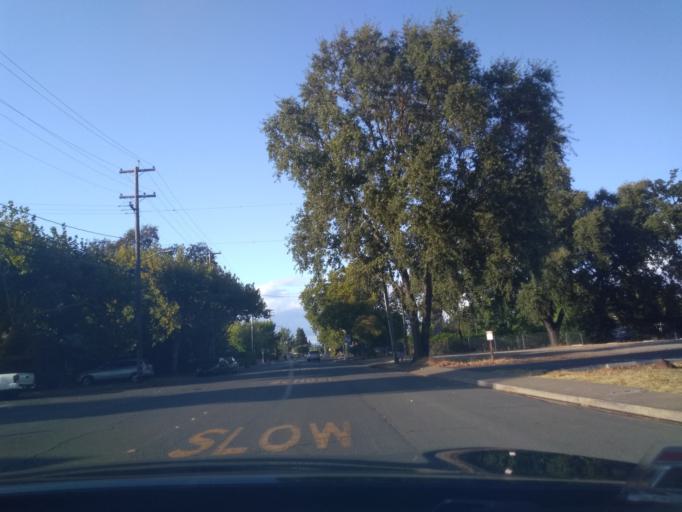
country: US
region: California
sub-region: Mendocino County
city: Ukiah
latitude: 39.1487
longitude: -123.1989
